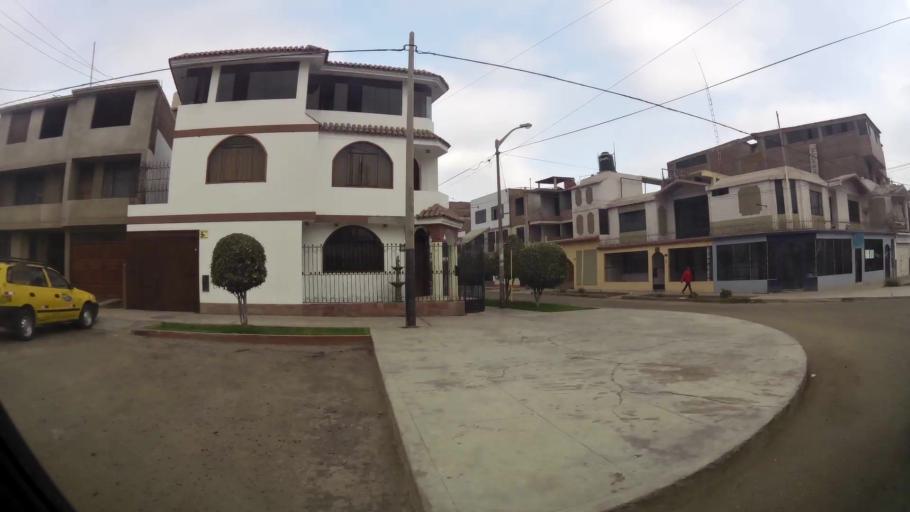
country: PE
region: La Libertad
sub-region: Provincia de Trujillo
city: Trujillo
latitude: -8.0973
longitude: -79.0224
